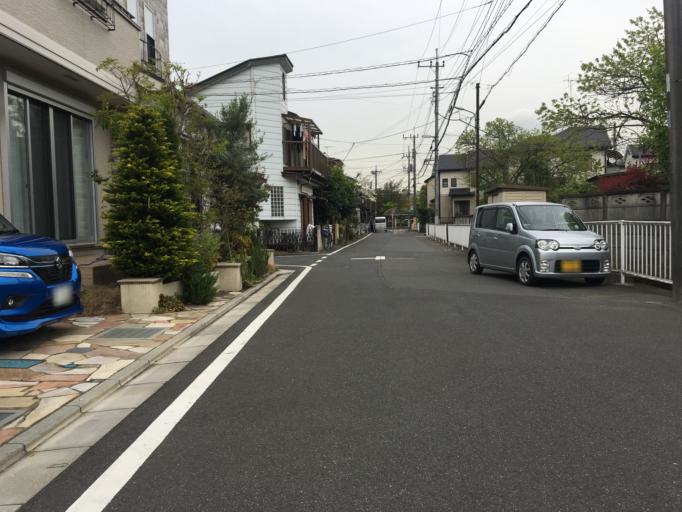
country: JP
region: Saitama
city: Oi
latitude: 35.8551
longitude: 139.5485
